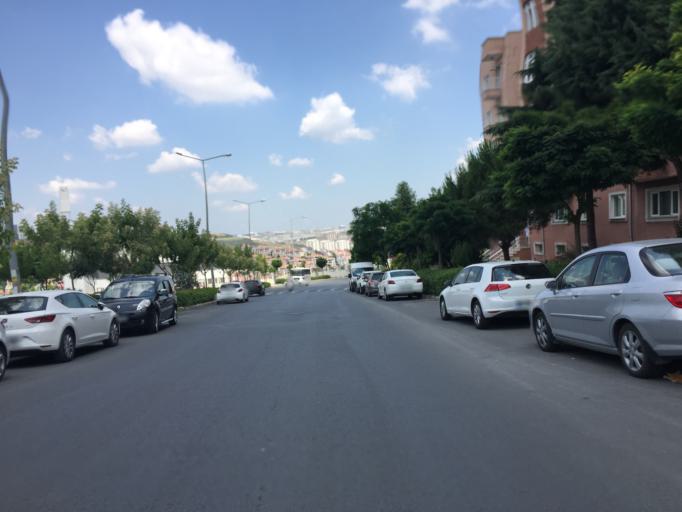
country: TR
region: Istanbul
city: Esenyurt
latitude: 41.0772
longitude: 28.6667
